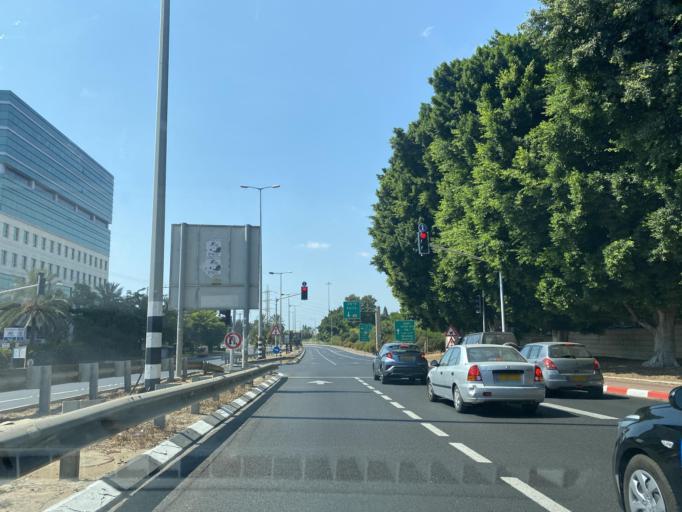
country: IL
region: Central District
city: Kfar Saba
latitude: 32.1759
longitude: 34.8909
